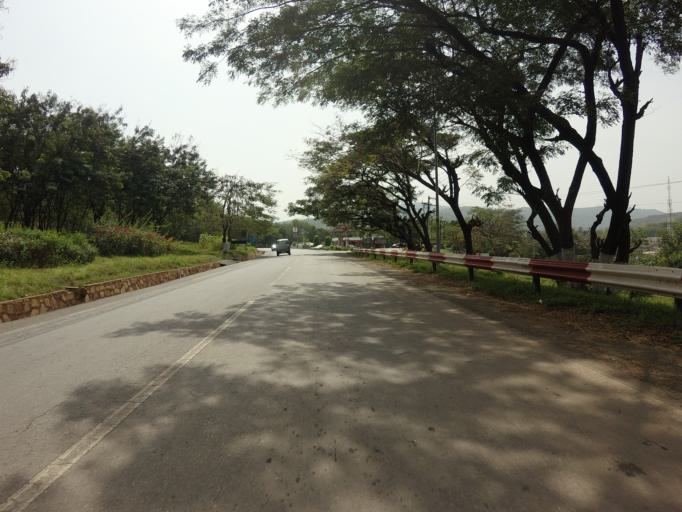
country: GH
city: Akropong
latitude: 6.2729
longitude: 0.0536
